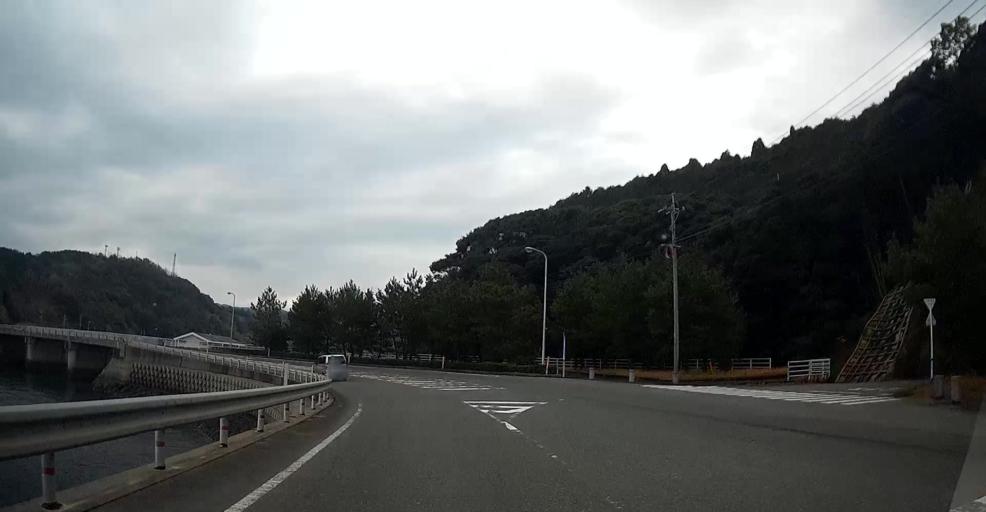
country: JP
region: Kumamoto
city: Hondo
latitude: 32.4867
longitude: 130.2868
